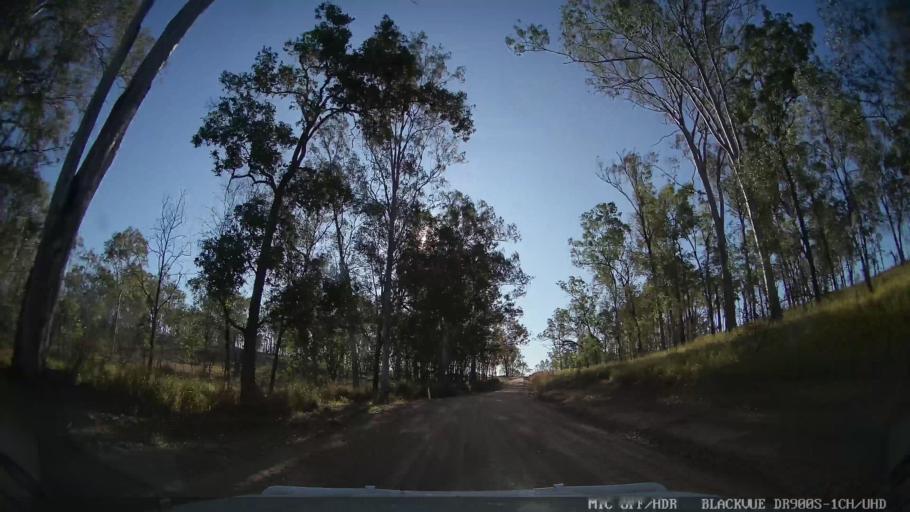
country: AU
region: Queensland
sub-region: Bundaberg
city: Sharon
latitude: -24.7912
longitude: 151.6095
